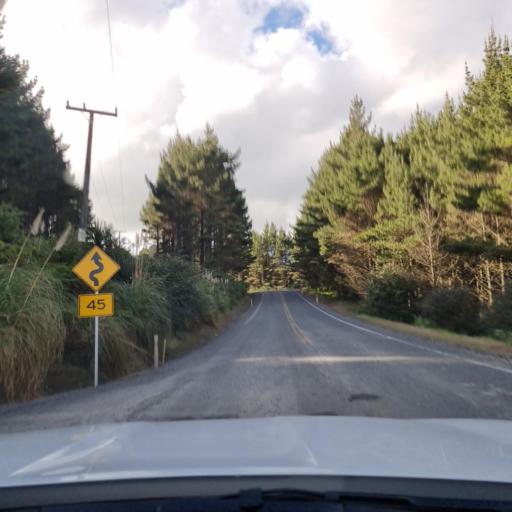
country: NZ
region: Northland
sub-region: Kaipara District
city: Dargaville
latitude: -36.2466
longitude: 174.0435
